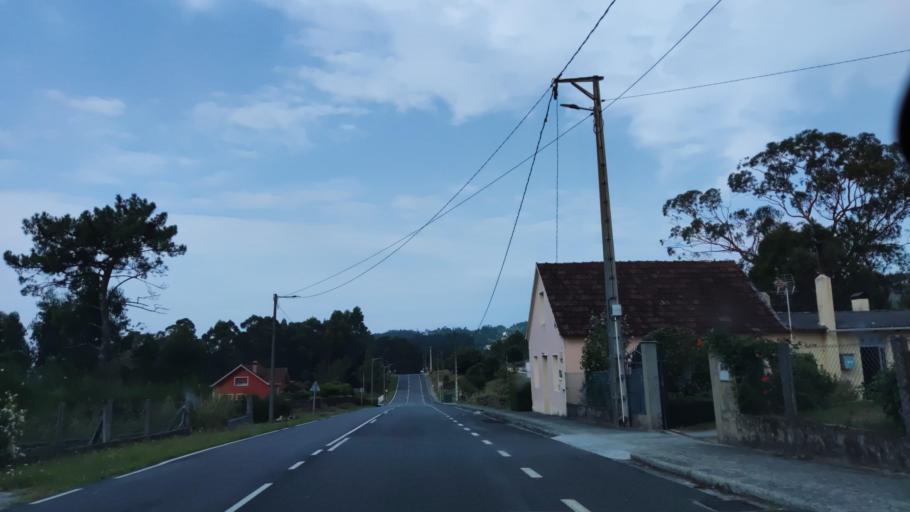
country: ES
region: Galicia
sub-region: Provincia de Pontevedra
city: Catoira
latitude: 42.6546
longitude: -8.7626
